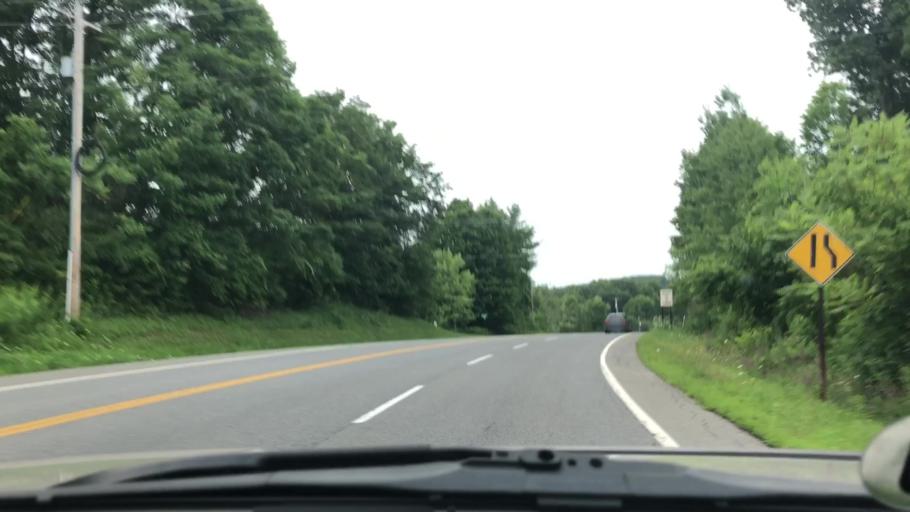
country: US
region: New York
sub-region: Saratoga County
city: Corinth
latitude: 43.1818
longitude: -73.7502
